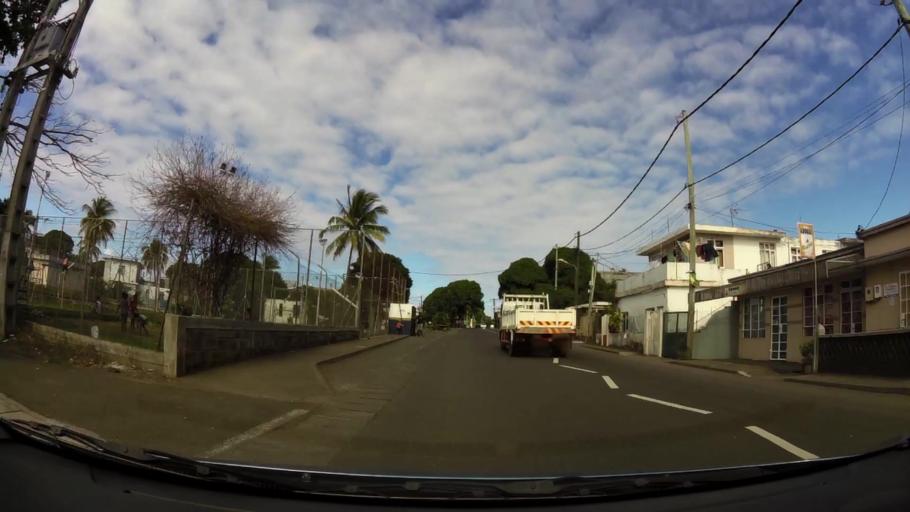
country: MU
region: Grand Port
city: Beau Vallon
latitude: -20.4193
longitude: 57.7036
